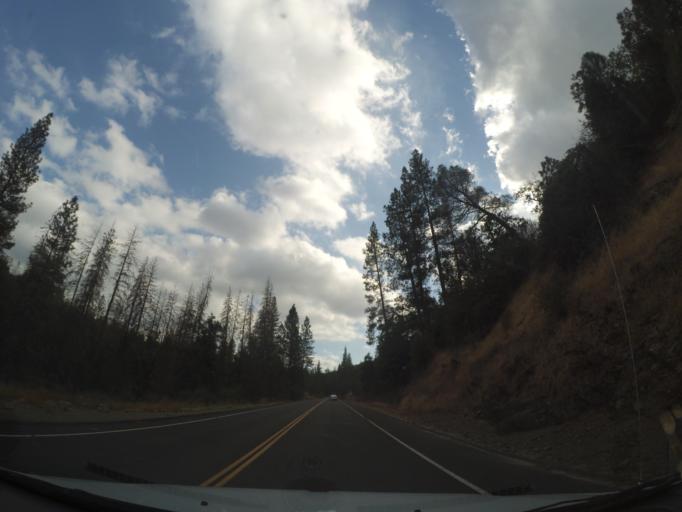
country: US
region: California
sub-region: Mariposa County
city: Midpines
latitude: 37.5357
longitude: -119.9200
